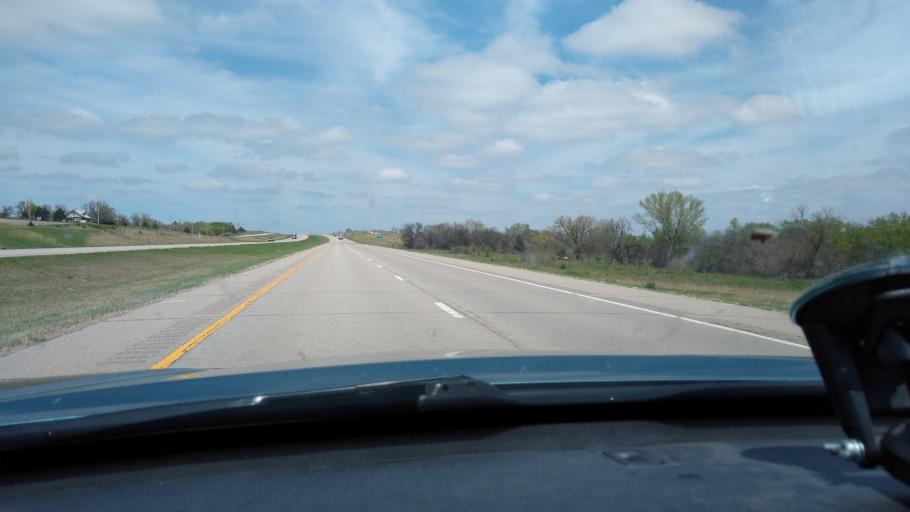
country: US
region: Kansas
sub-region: Cloud County
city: Concordia
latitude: 39.5180
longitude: -97.6564
